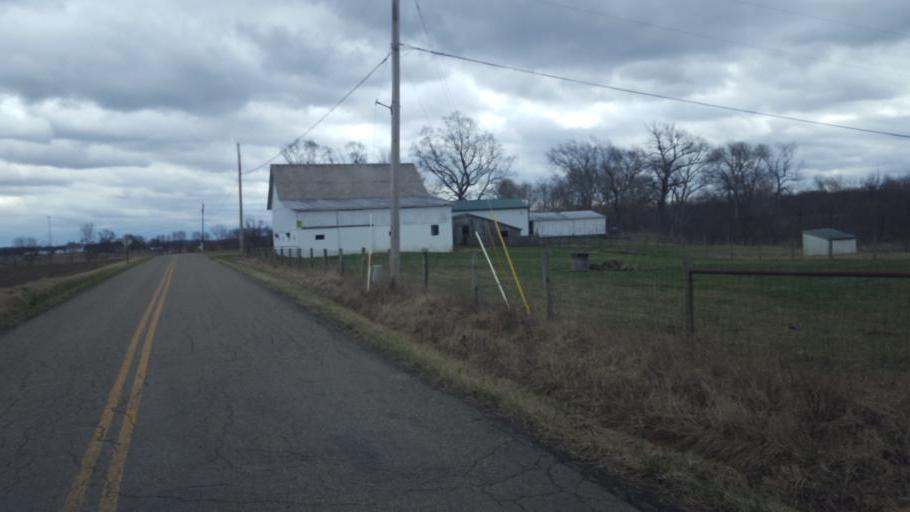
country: US
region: Ohio
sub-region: Licking County
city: Utica
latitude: 40.2676
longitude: -82.4979
